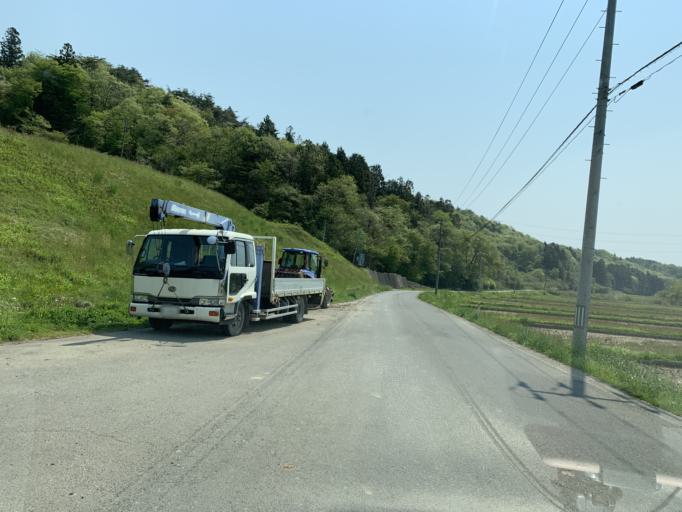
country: JP
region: Iwate
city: Ichinoseki
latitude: 38.8476
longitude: 141.0650
